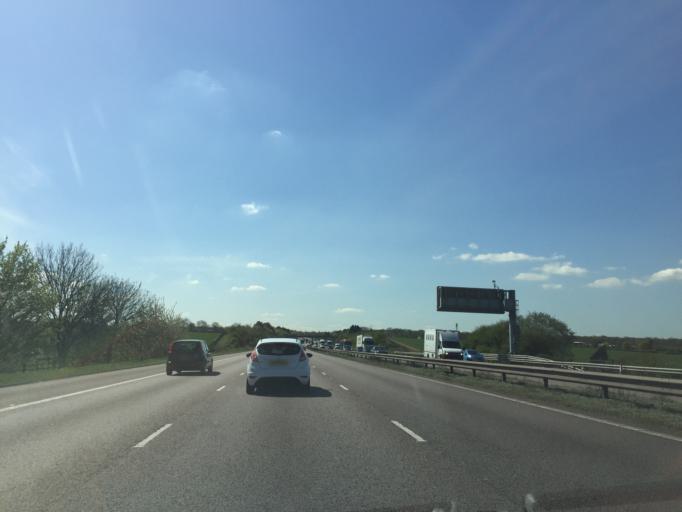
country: GB
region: England
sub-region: Essex
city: Epping
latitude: 51.7284
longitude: 0.1404
